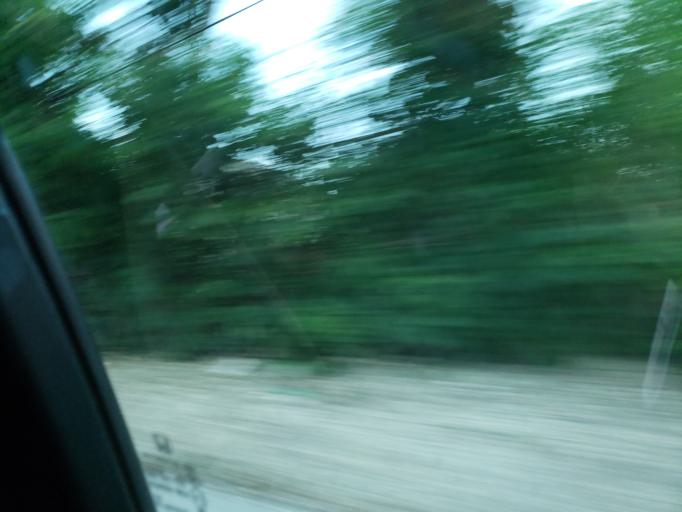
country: ID
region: Bali
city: Kangin
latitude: -8.8308
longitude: 115.1286
